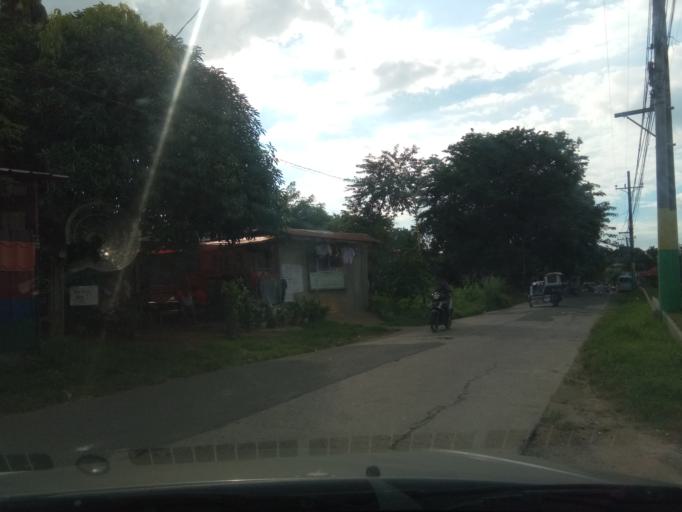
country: PH
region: Calabarzon
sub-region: Province of Cavite
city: Biga
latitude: 14.2812
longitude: 120.9467
